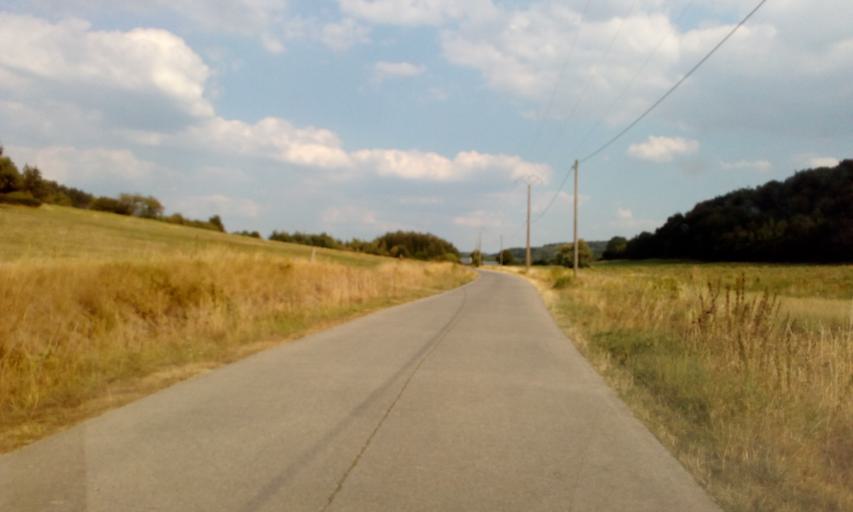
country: BE
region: Wallonia
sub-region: Province du Luxembourg
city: Tellin
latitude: 50.1103
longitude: 5.1799
